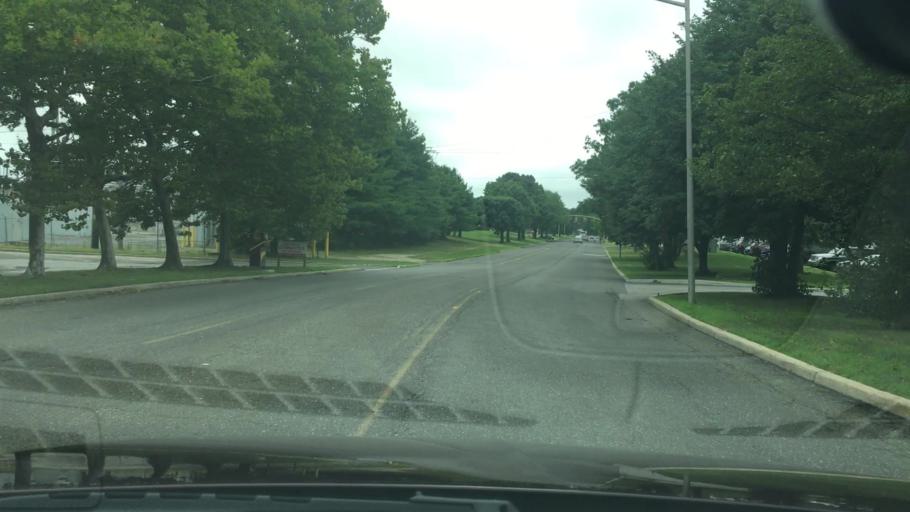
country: US
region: New York
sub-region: Suffolk County
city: Commack
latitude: 40.8160
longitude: -73.2702
